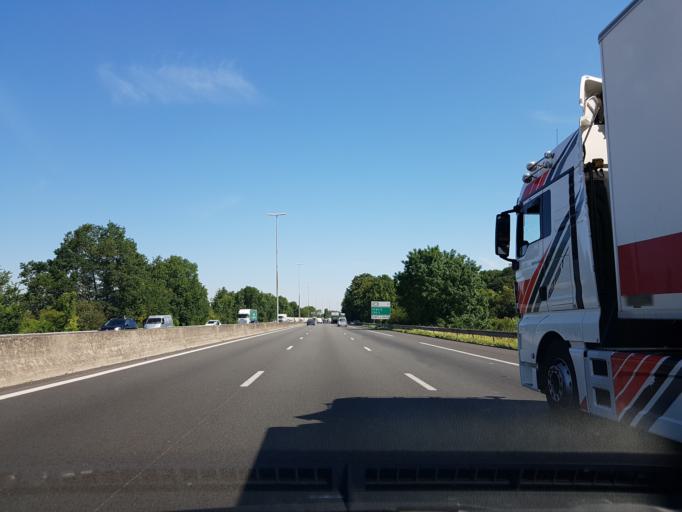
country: FR
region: Ile-de-France
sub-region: Departement du Val-d'Oise
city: Survilliers
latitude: 49.0941
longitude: 2.5504
